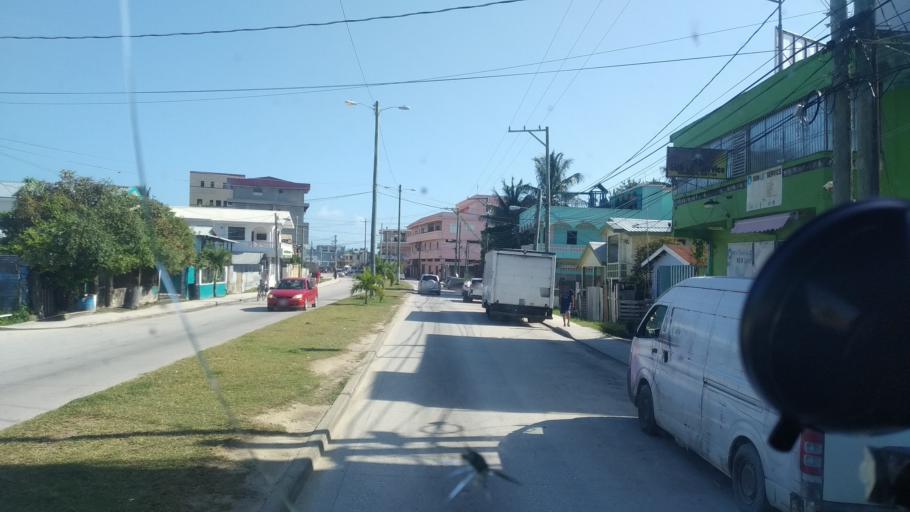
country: BZ
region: Belize
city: Belize City
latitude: 17.4890
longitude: -88.2001
